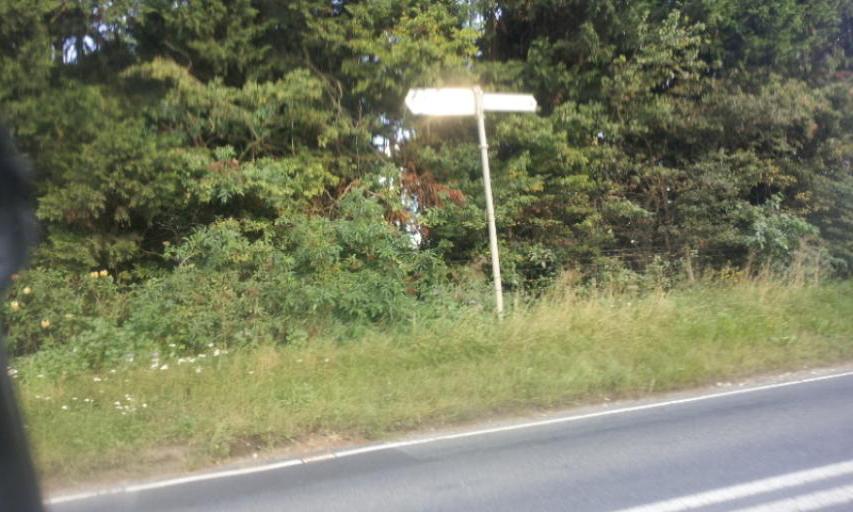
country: GB
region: England
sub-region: Kent
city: Longfield
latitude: 51.4071
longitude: 0.2821
